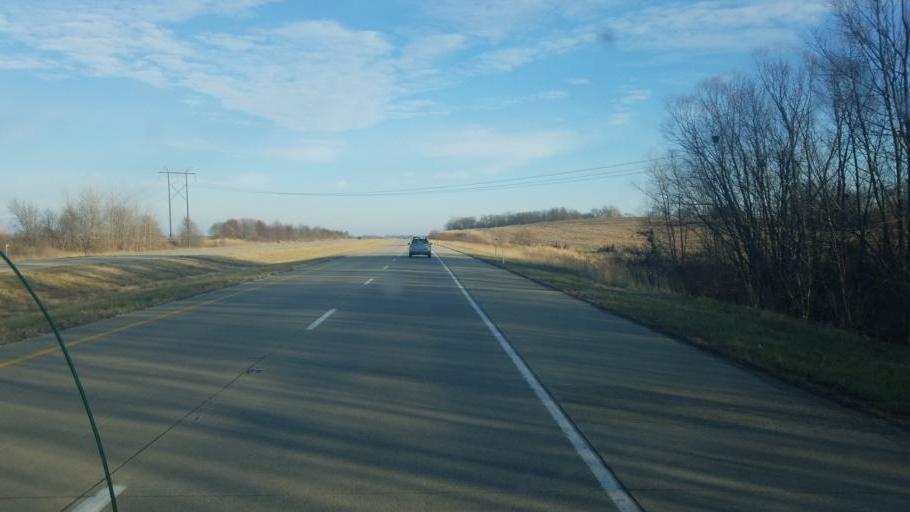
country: US
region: Indiana
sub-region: Knox County
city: Vincennes
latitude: 38.6785
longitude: -87.3987
